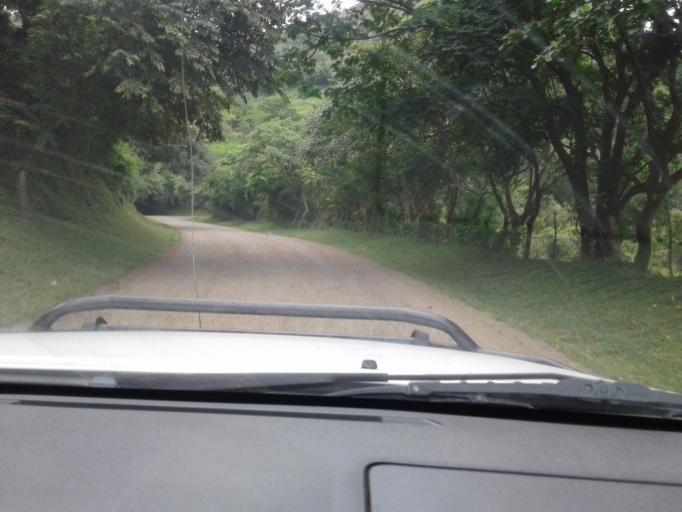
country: NI
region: Matagalpa
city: San Ramon
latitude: 12.9119
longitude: -85.8103
